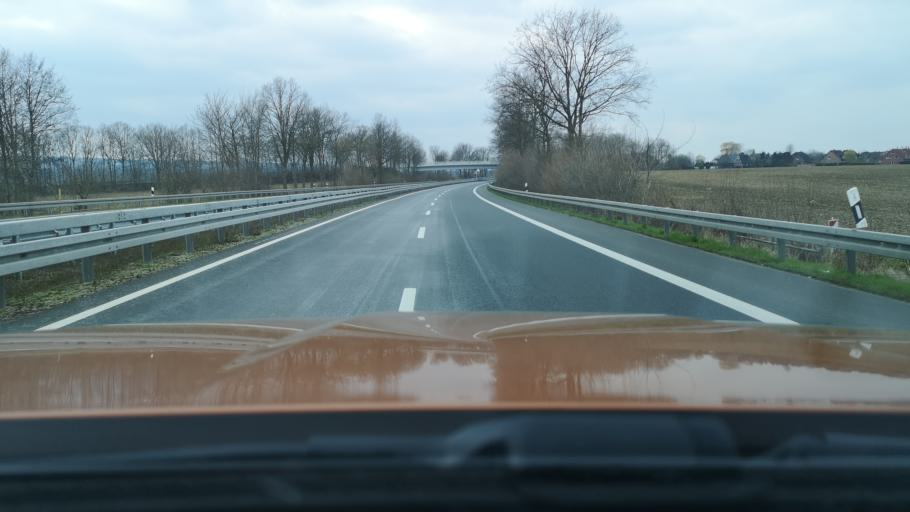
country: DE
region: Lower Saxony
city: Stadthagen
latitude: 52.3141
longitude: 9.2207
